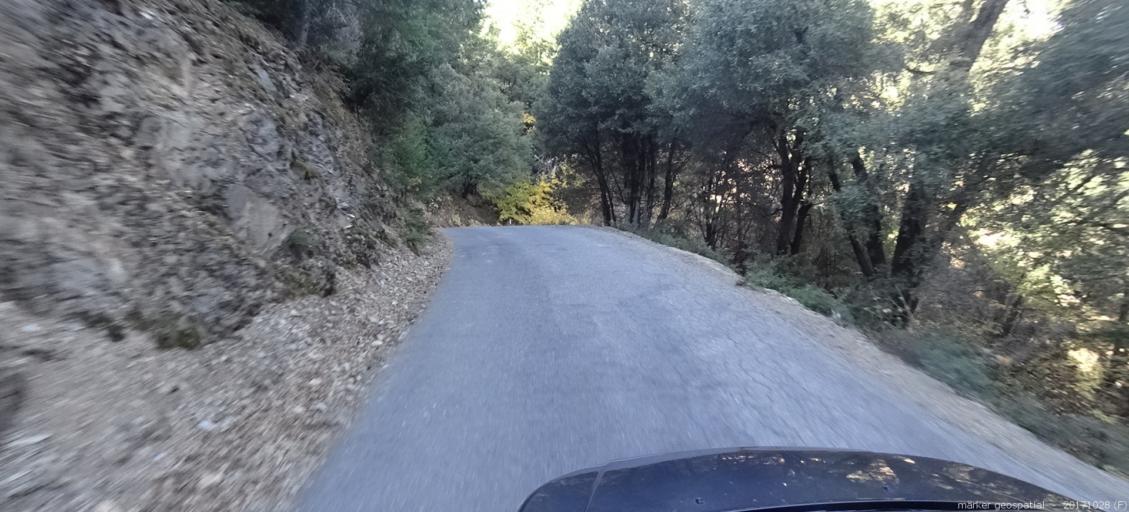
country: US
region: California
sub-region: Trinity County
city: Lewiston
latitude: 40.8116
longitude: -122.6331
